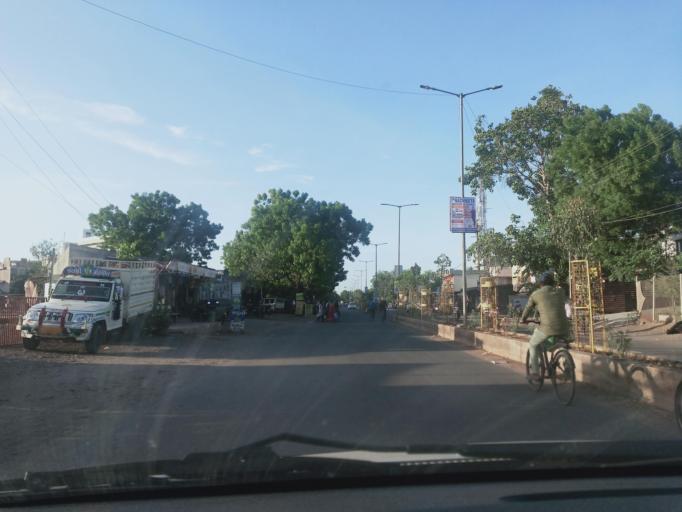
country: IN
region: Gujarat
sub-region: Bhavnagar
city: Bhavnagar
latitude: 21.7392
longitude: 72.1483
